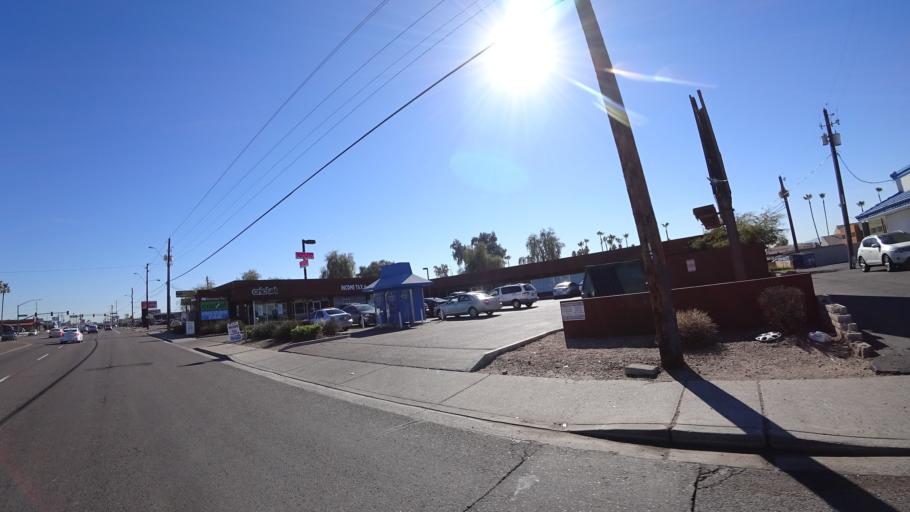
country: US
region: Arizona
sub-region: Maricopa County
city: Glendale
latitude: 33.4948
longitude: -112.1538
